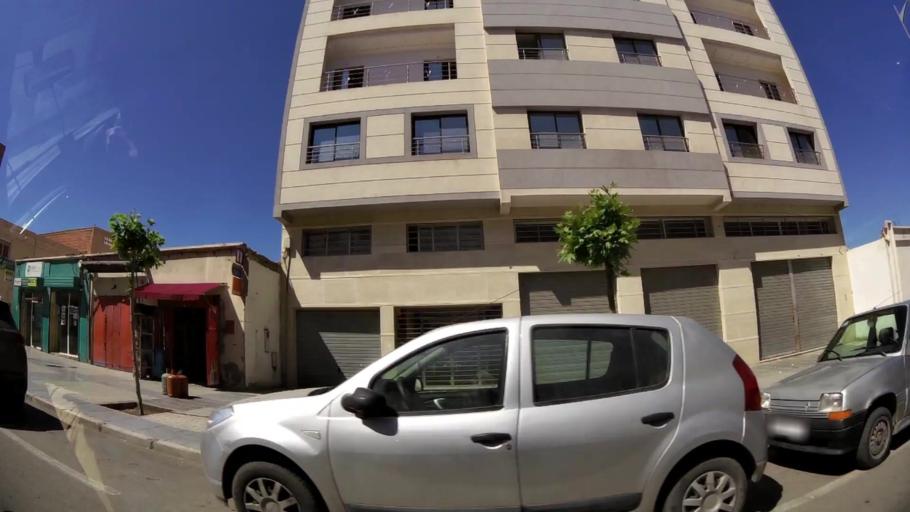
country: MA
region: Oriental
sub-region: Oujda-Angad
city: Oujda
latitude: 34.6804
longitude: -1.9341
